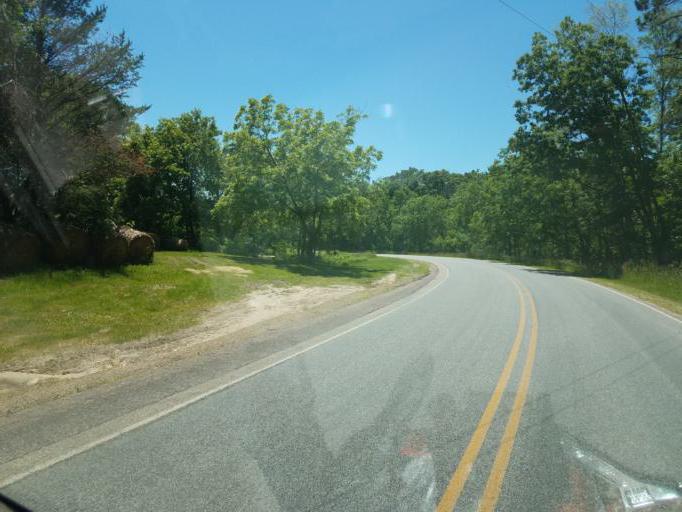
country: US
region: Wisconsin
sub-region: Juneau County
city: New Lisbon
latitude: 43.8637
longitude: -90.2859
